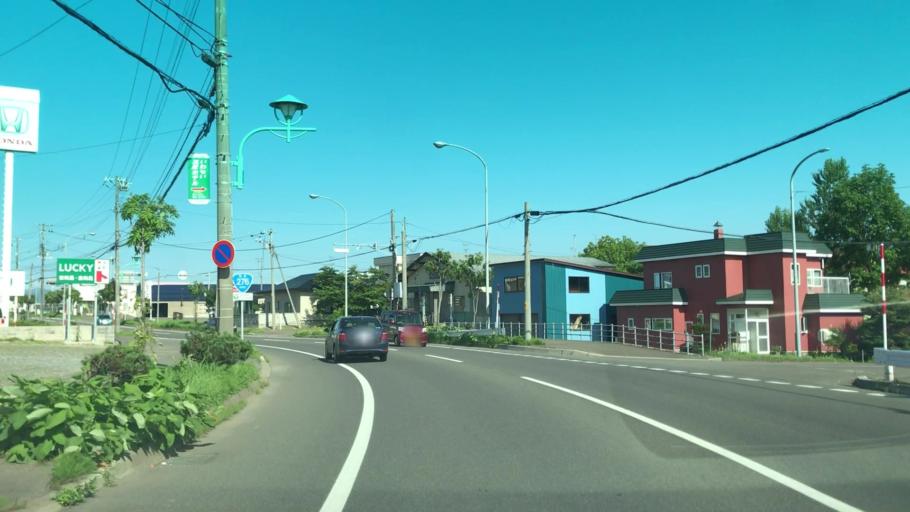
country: JP
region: Hokkaido
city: Iwanai
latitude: 42.9811
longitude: 140.5401
